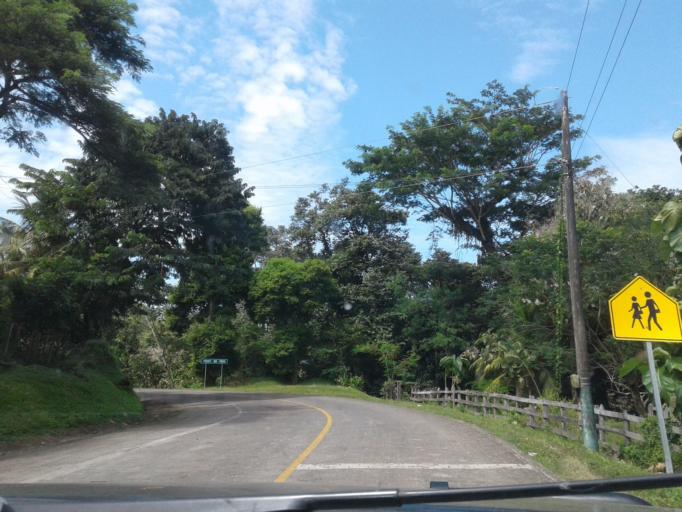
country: NI
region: Rivas
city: Cardenas
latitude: 11.1836
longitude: -85.4908
